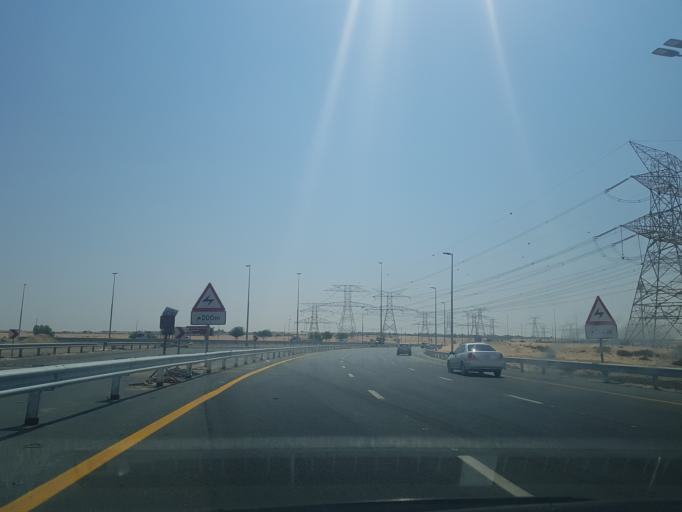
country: AE
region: Ash Shariqah
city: Sharjah
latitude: 25.2357
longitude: 55.5638
